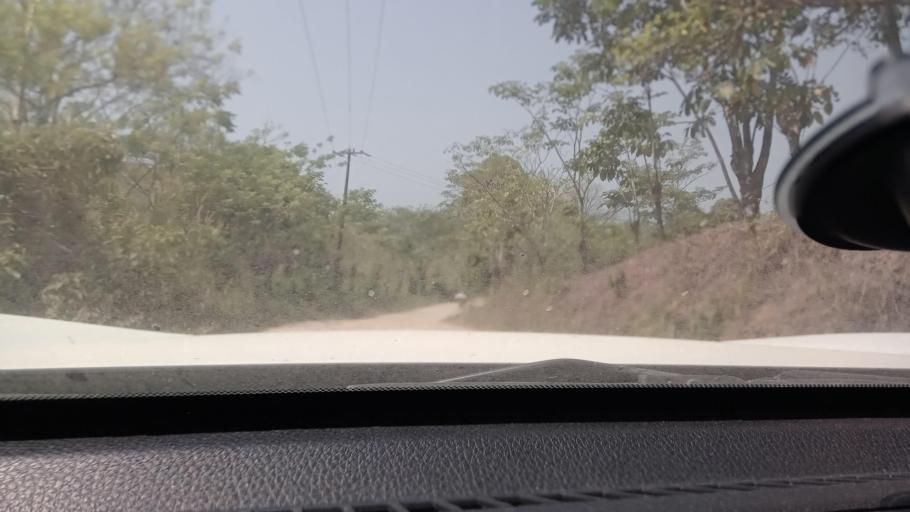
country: MX
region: Tabasco
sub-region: Huimanguillo
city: Francisco Rueda
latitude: 17.5168
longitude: -93.8898
